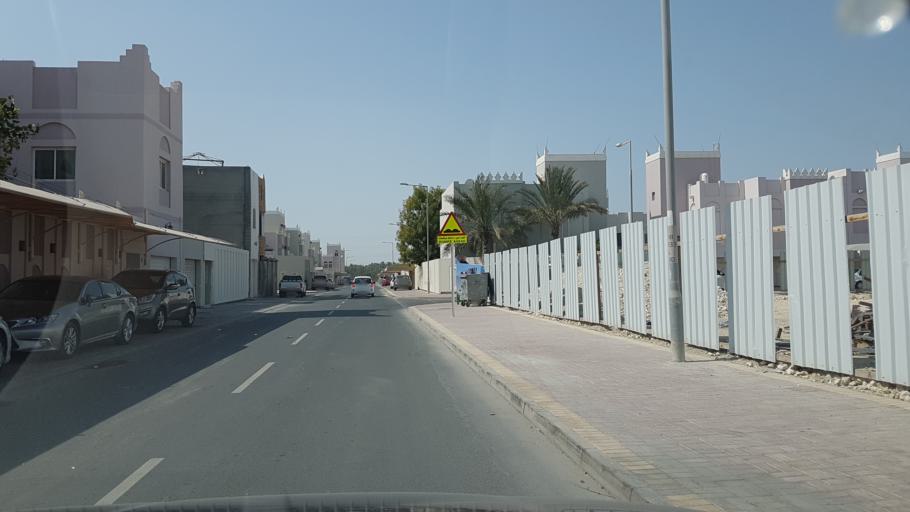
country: BH
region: Northern
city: Madinat `Isa
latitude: 26.1668
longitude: 50.5390
